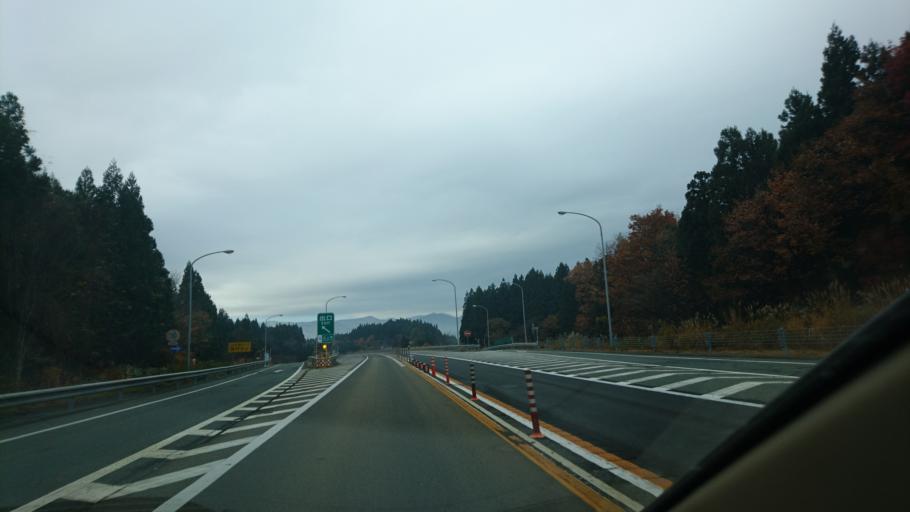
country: JP
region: Iwate
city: Kitakami
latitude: 39.2908
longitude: 140.9872
